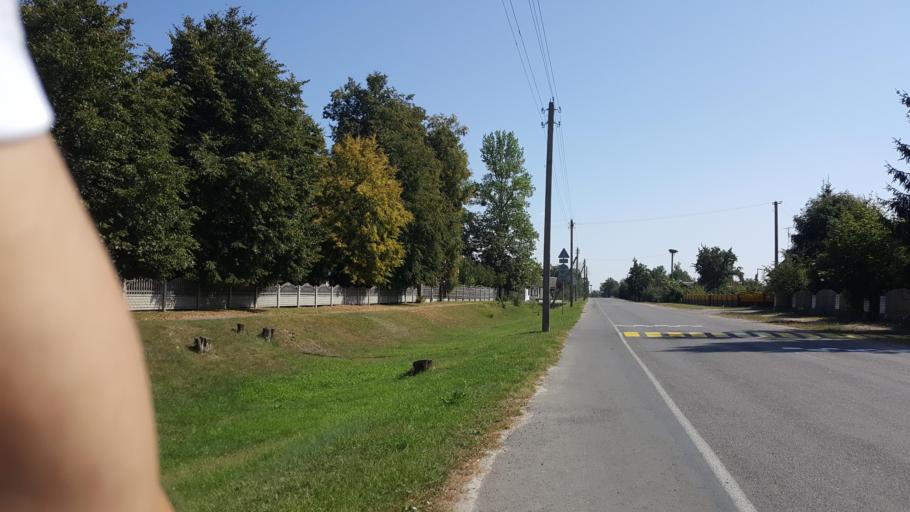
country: PL
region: Podlasie
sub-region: Powiat hajnowski
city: Czeremcha
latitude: 52.4738
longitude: 23.5064
